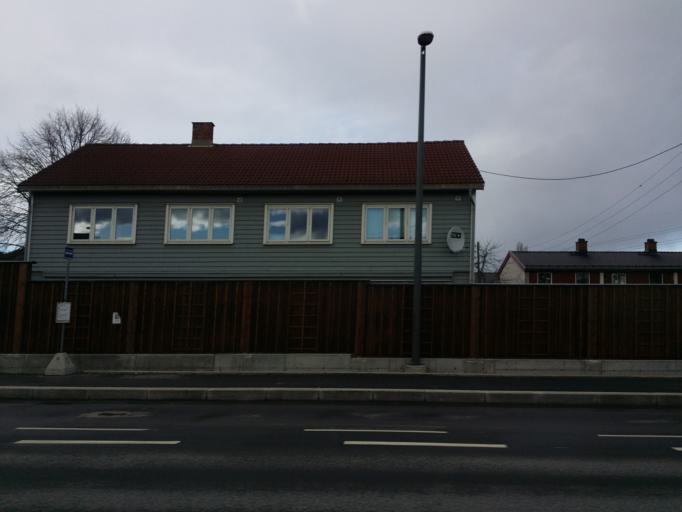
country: NO
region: Oslo
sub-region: Oslo
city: Oslo
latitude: 59.9328
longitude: 10.7977
